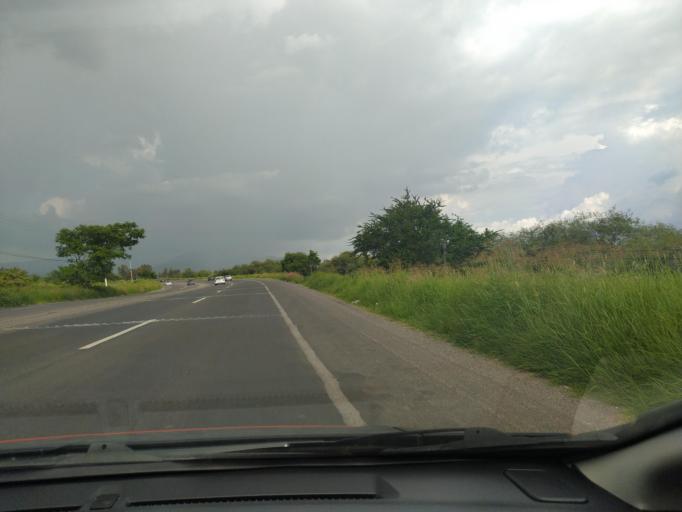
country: MX
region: Jalisco
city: Villa Corona
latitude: 20.4088
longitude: -103.6543
